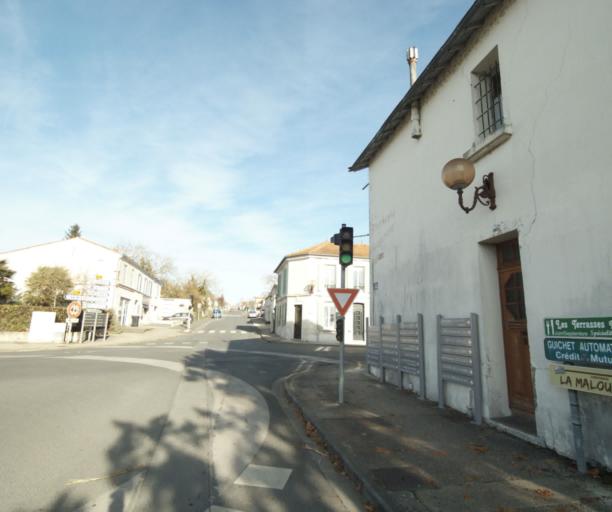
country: FR
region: Poitou-Charentes
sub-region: Departement de la Charente-Maritime
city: Chaniers
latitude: 45.7180
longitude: -0.5576
